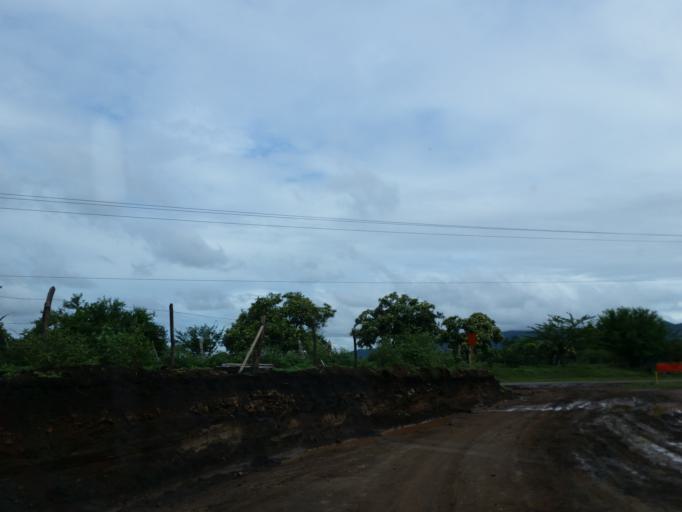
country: NI
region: Leon
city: Larreynaga
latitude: 12.6053
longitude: -86.6706
